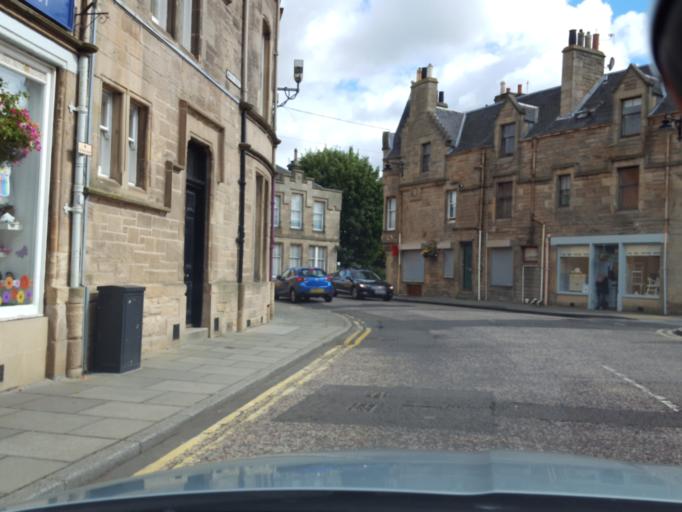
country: GB
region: Scotland
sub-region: Falkirk
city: Bo'ness
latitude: 56.0176
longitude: -3.6087
